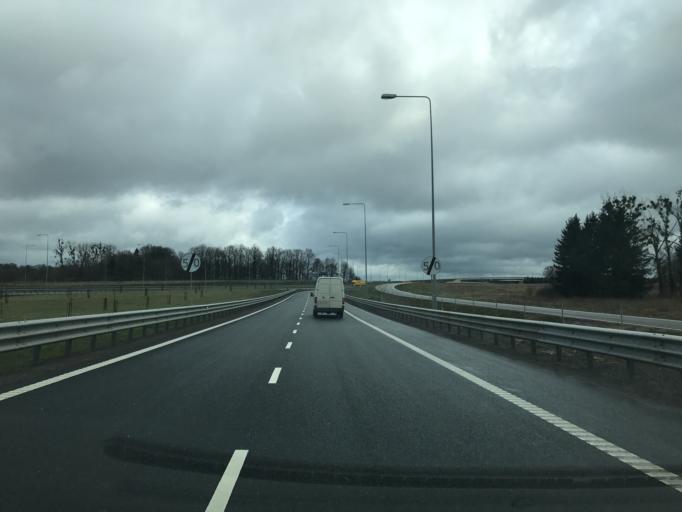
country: PL
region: Warmian-Masurian Voivodeship
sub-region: Powiat olsztynski
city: Olsztynek
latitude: 53.5799
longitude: 20.2535
